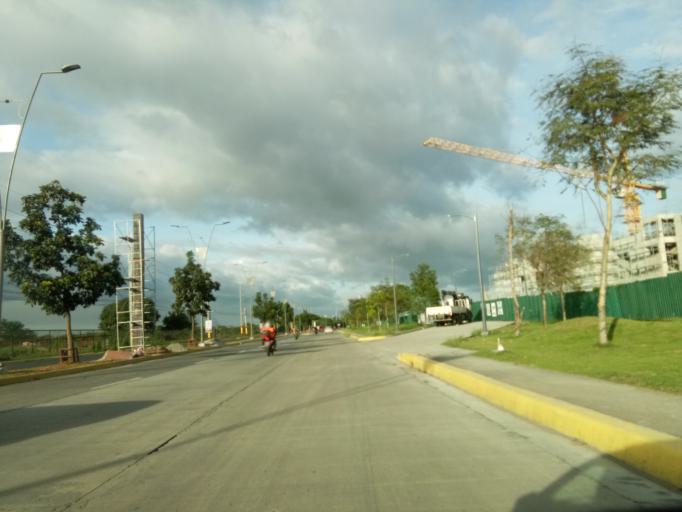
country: PH
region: Calabarzon
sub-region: Province of Cavite
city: Imus
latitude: 14.3837
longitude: 120.9590
